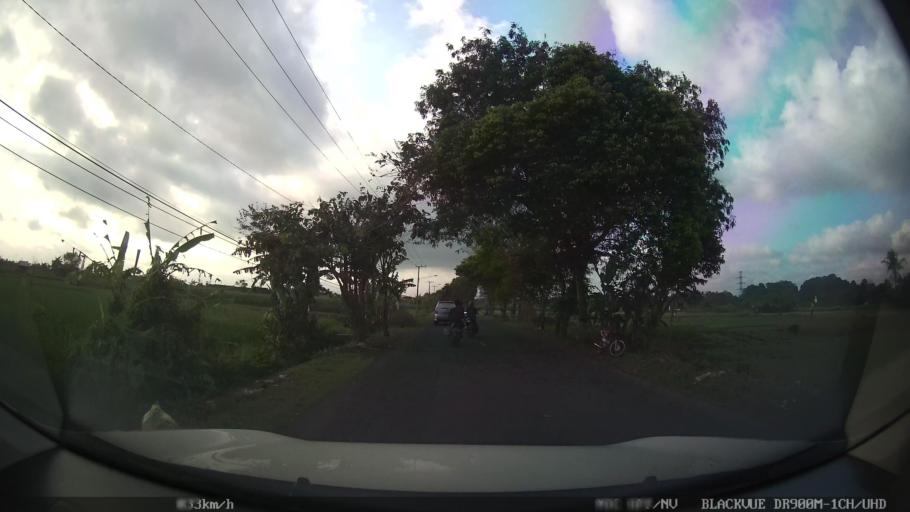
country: ID
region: Bali
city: Banjar Sedang
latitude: -8.5589
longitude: 115.2336
